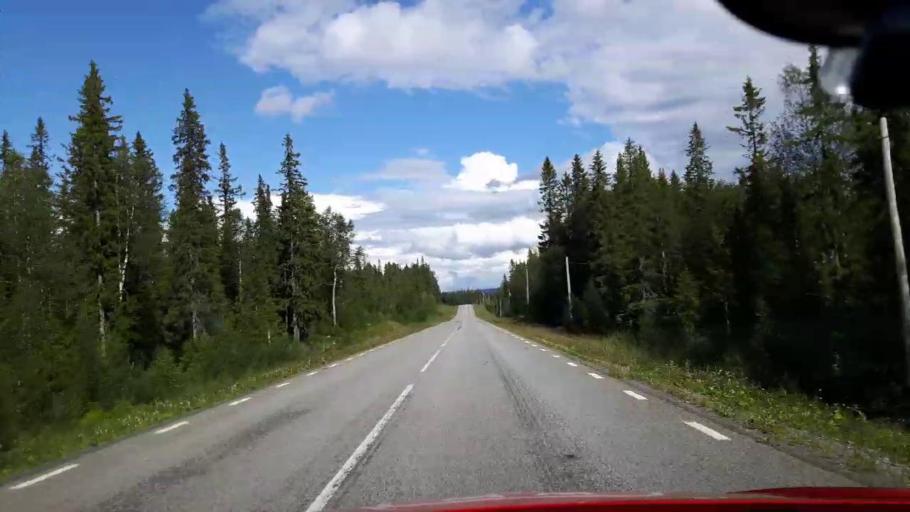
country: SE
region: Jaemtland
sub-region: Are Kommun
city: Are
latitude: 63.2241
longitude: 13.1304
